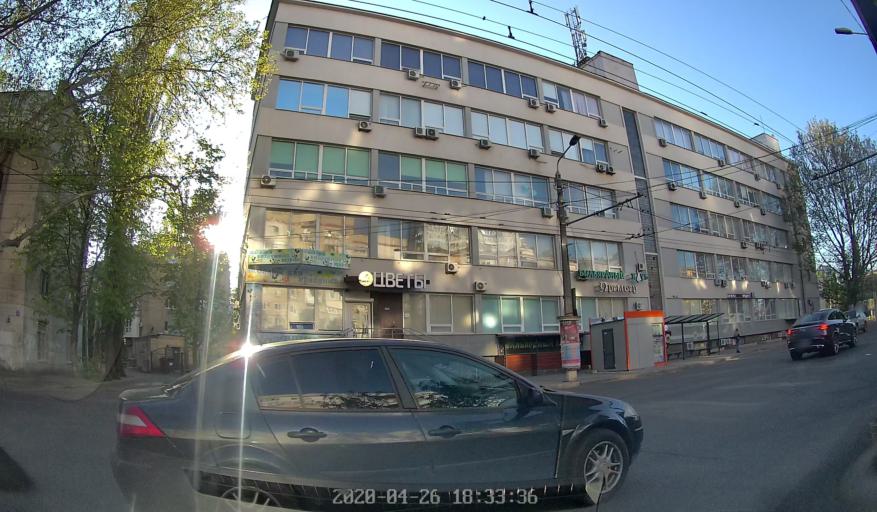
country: NG
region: Niger
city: Lemu
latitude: 9.2907
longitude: 6.1489
